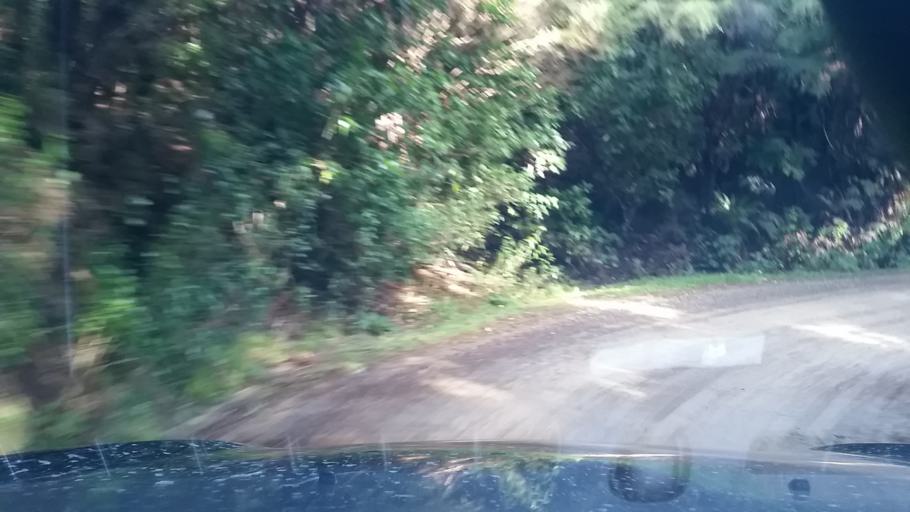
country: NZ
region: Marlborough
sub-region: Marlborough District
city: Picton
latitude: -41.1603
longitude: 173.9716
